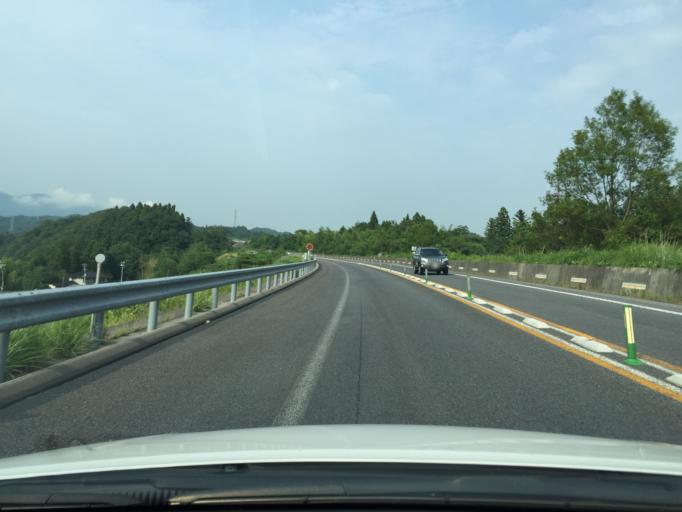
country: JP
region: Fukushima
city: Iwaki
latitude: 37.0982
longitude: 140.8706
